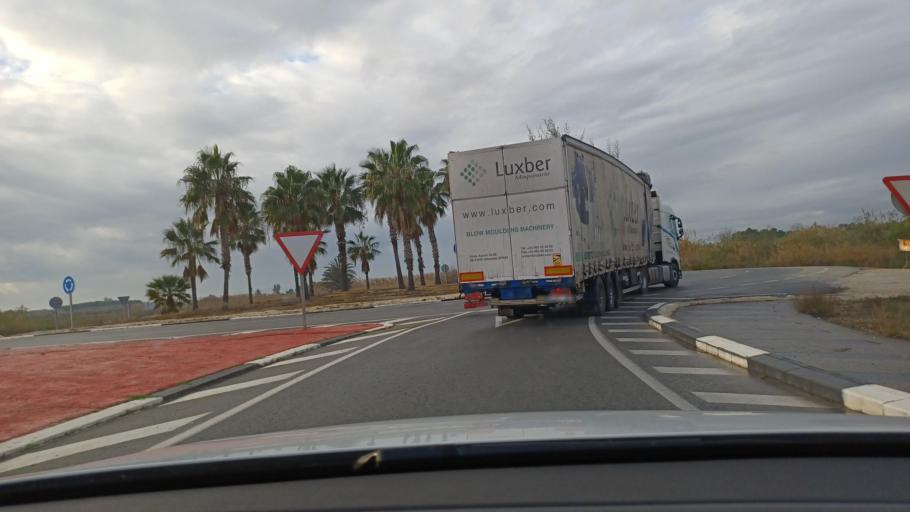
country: ES
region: Valencia
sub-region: Provincia de Alicante
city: Daya Vieja
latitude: 38.1594
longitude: -0.7032
